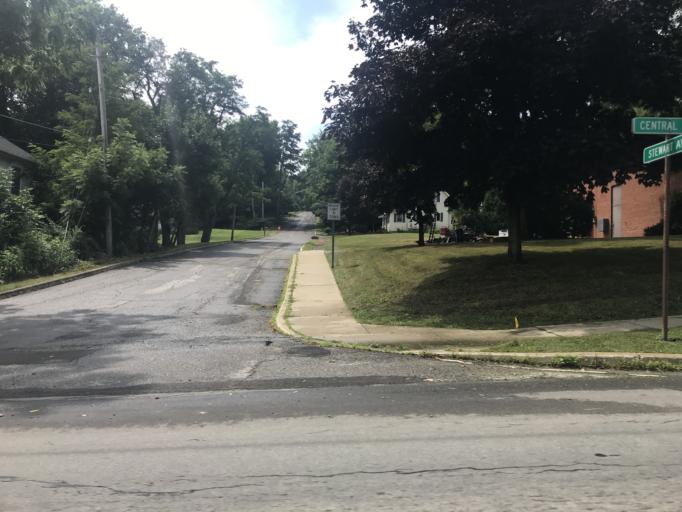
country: US
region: New York
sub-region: Chautauqua County
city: Silver Creek
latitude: 42.5456
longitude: -79.1727
